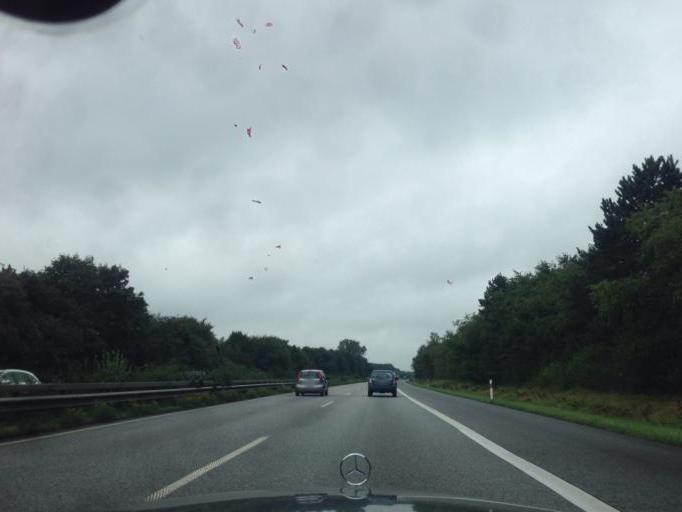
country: DE
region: Schleswig-Holstein
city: Eisendorf
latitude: 54.2034
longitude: 9.8757
